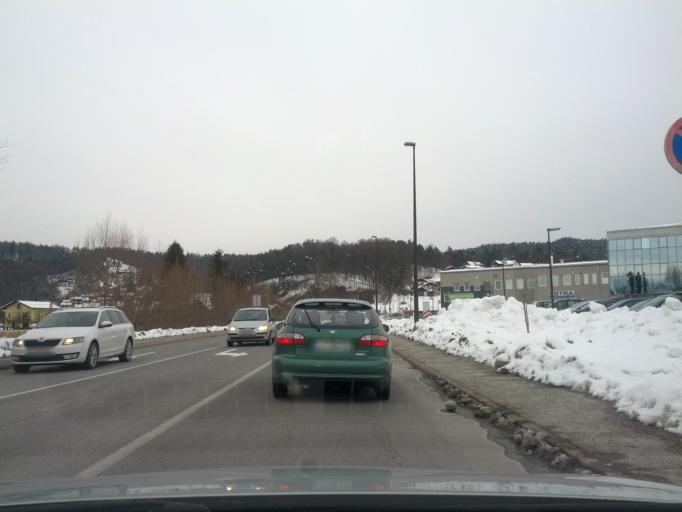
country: SI
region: Skofljica
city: Lavrica
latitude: 46.0236
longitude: 14.5358
